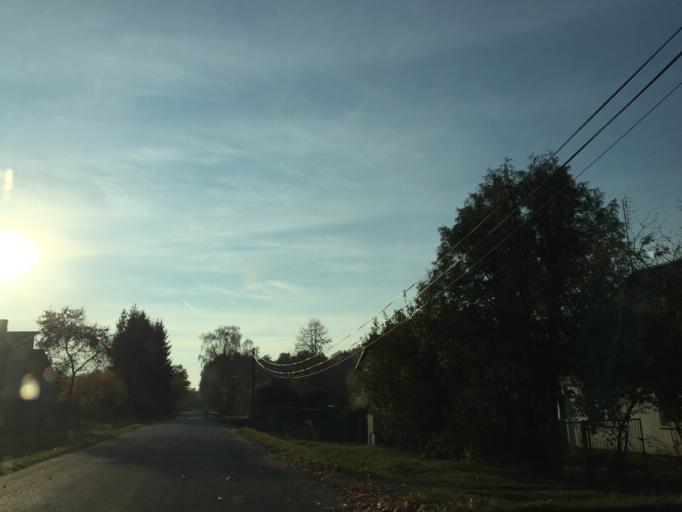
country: LV
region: Skrunda
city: Skrunda
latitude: 56.6762
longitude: 22.0103
